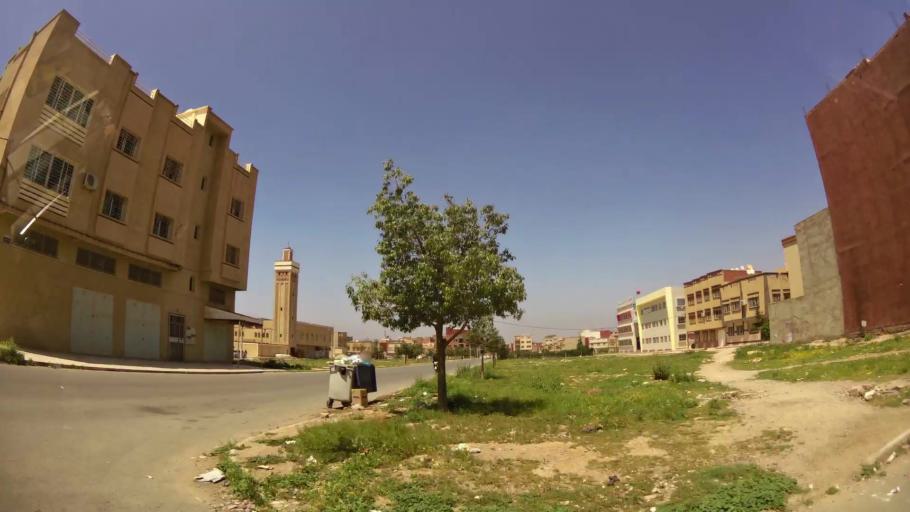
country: MA
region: Oriental
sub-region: Oujda-Angad
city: Oujda
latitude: 34.6937
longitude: -1.8878
